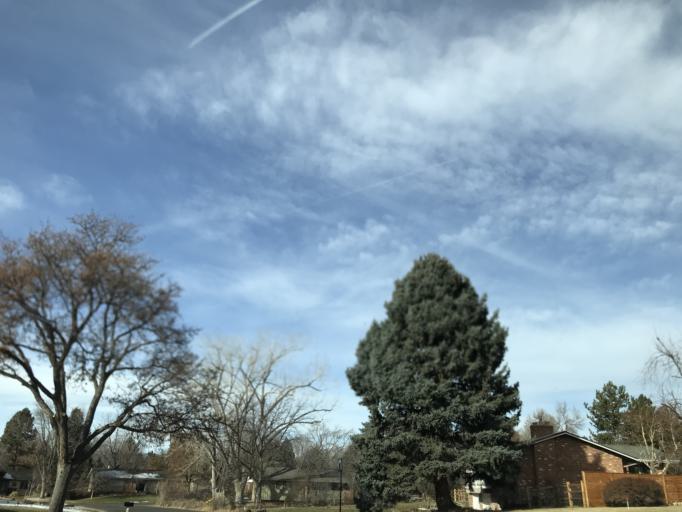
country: US
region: Colorado
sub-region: Arapahoe County
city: Littleton
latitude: 39.5978
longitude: -105.0126
